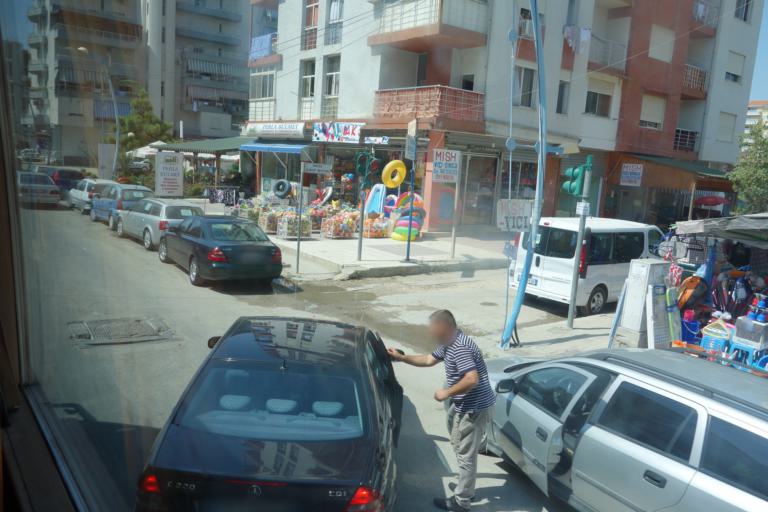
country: AL
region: Durres
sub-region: Rrethi i Durresit
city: Rrashbull
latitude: 41.3074
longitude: 19.4905
